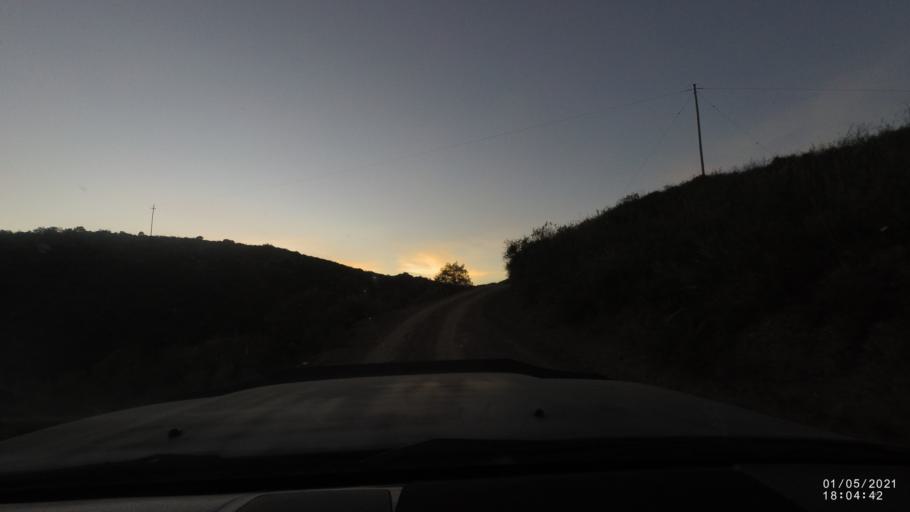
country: BO
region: Cochabamba
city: Capinota
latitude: -17.6892
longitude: -66.1800
